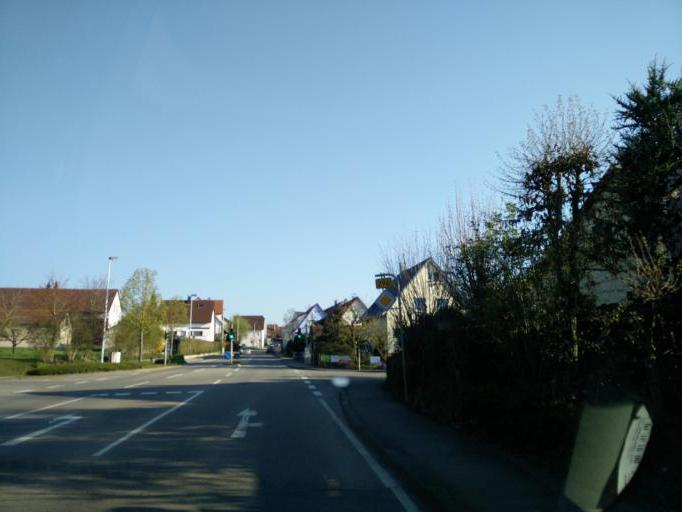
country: DE
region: Baden-Wuerttemberg
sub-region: Regierungsbezirk Stuttgart
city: Herrenberg
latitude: 48.6044
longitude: 8.8601
